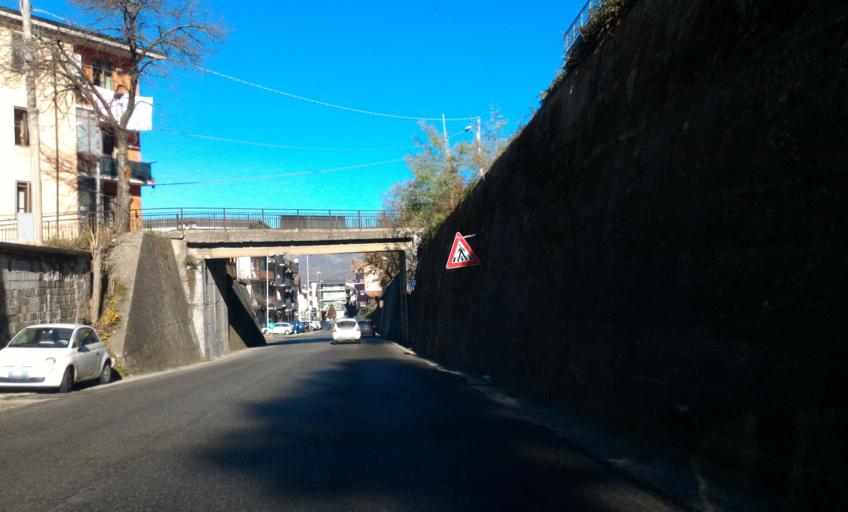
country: IT
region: Calabria
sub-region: Provincia di Cosenza
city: Spezzano della Sila
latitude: 39.3011
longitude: 16.3407
